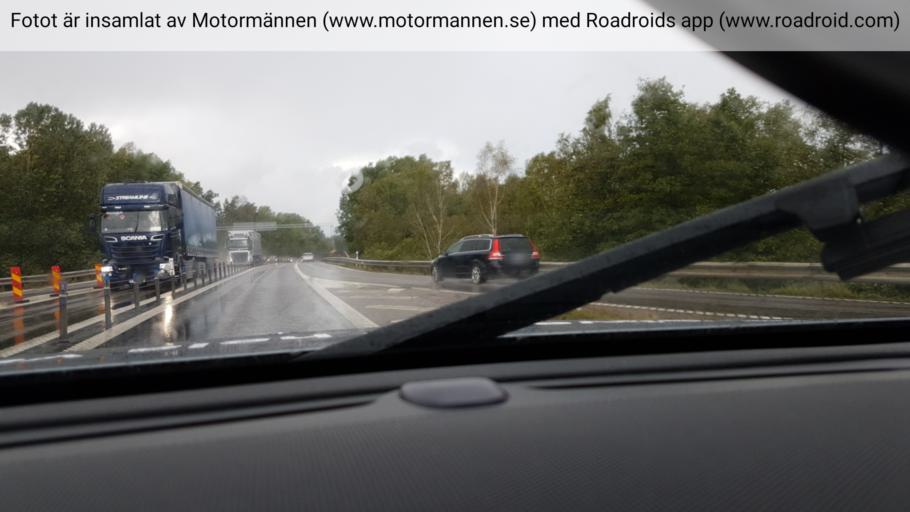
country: SE
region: Vaestra Goetaland
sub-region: Trollhattan
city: Trollhattan
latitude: 58.3182
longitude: 12.3047
